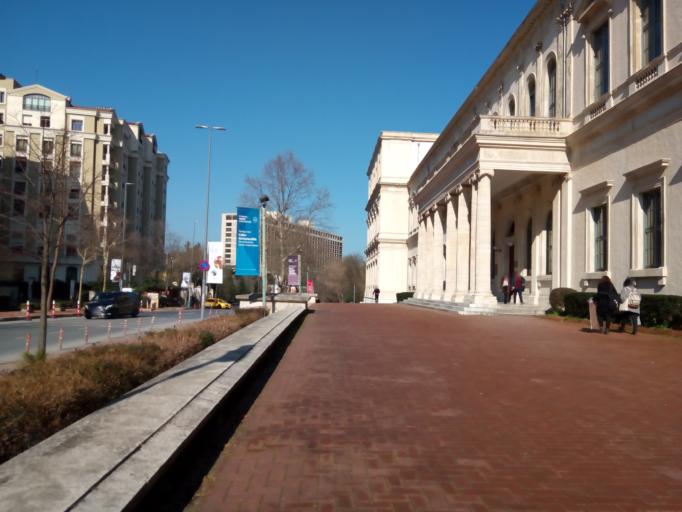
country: TR
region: Istanbul
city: Sisli
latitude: 41.0409
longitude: 28.9890
